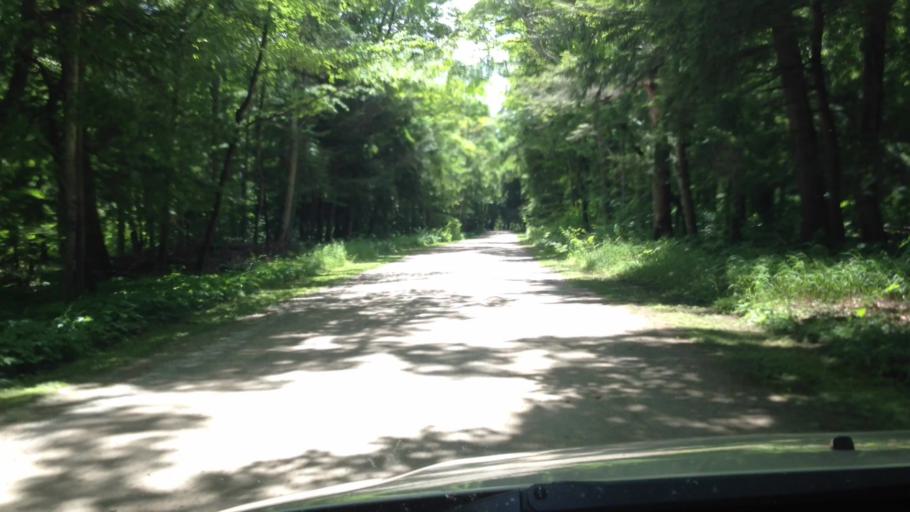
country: US
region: Michigan
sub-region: Menominee County
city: Menominee
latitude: 45.3968
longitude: -87.3643
